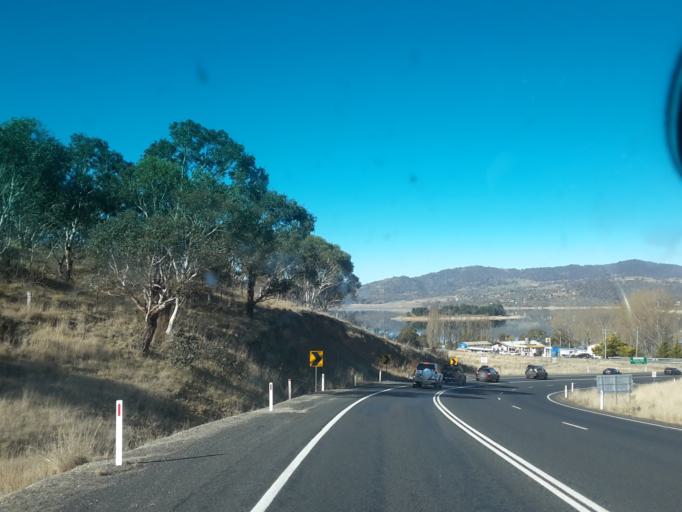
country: AU
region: New South Wales
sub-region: Snowy River
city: Jindabyne
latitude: -36.4102
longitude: 148.5930
